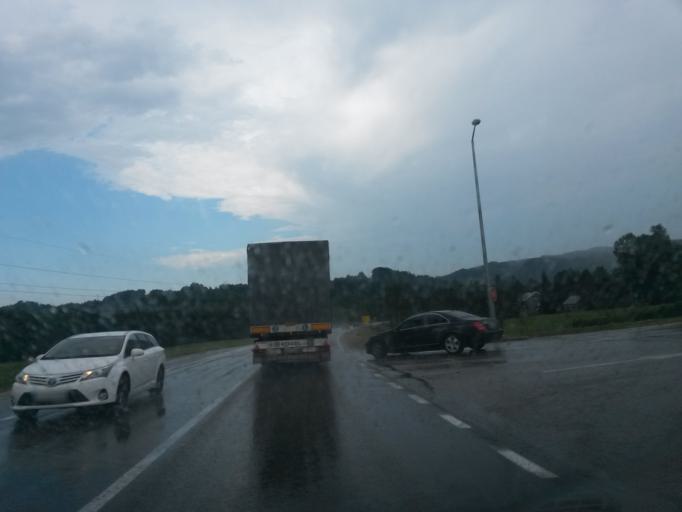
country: BA
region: Federation of Bosnia and Herzegovina
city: Lijesnica
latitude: 44.4816
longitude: 18.0687
